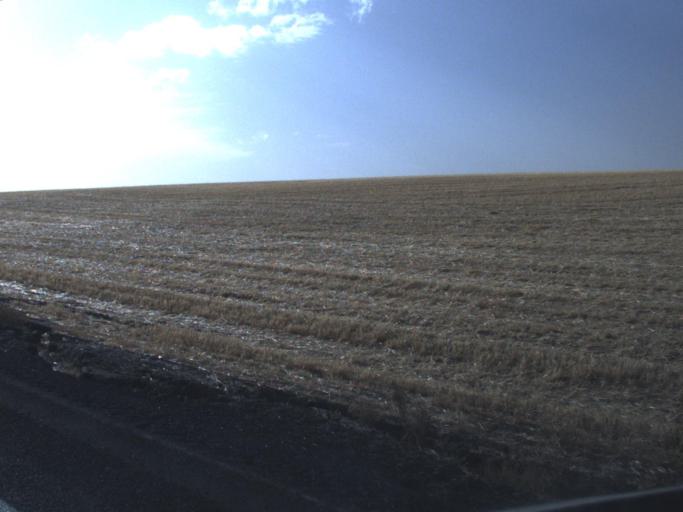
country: US
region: Washington
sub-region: Adams County
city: Ritzville
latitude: 47.4090
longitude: -118.3778
